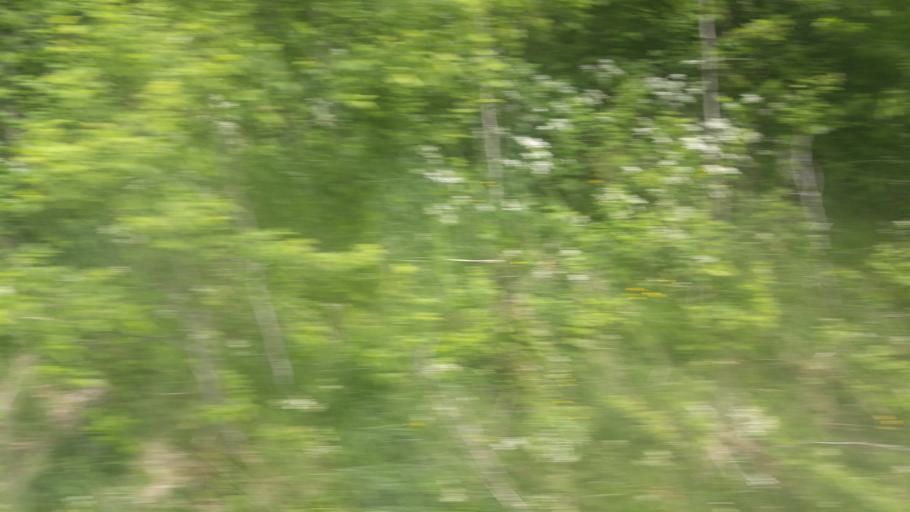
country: NO
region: Sor-Trondelag
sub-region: Midtre Gauldal
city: Storen
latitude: 62.9430
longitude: 10.6449
